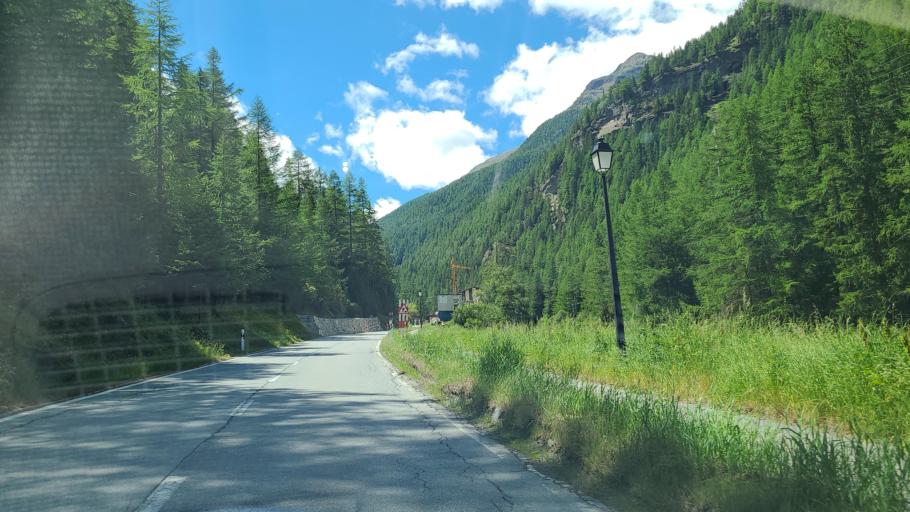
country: CH
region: Valais
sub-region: Visp District
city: Saas-Grund
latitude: 46.1505
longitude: 7.9280
